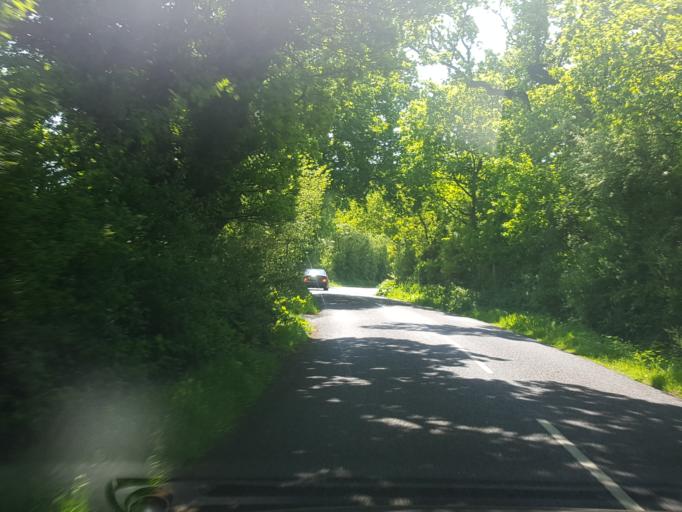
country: GB
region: England
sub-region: Essex
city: Great Bentley
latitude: 51.8596
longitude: 1.0912
